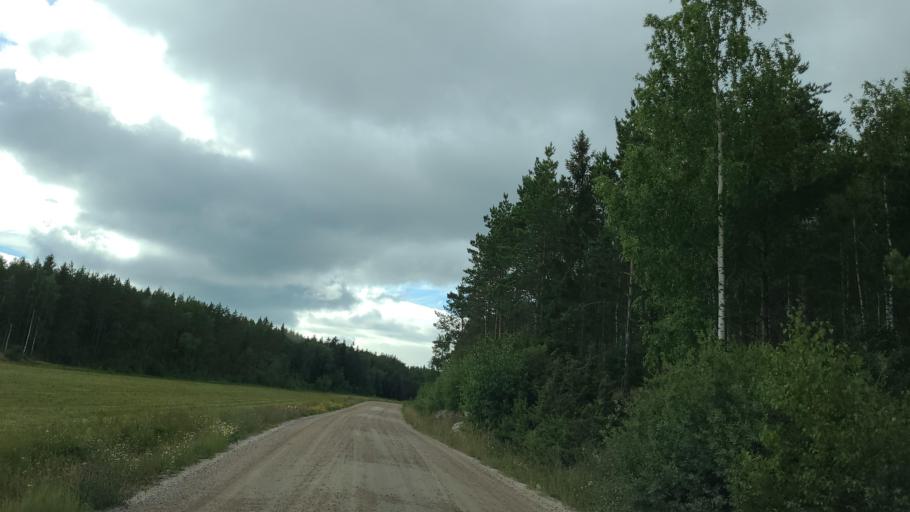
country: FI
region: Varsinais-Suomi
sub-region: Aboland-Turunmaa
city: Nagu
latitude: 60.2051
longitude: 21.8559
